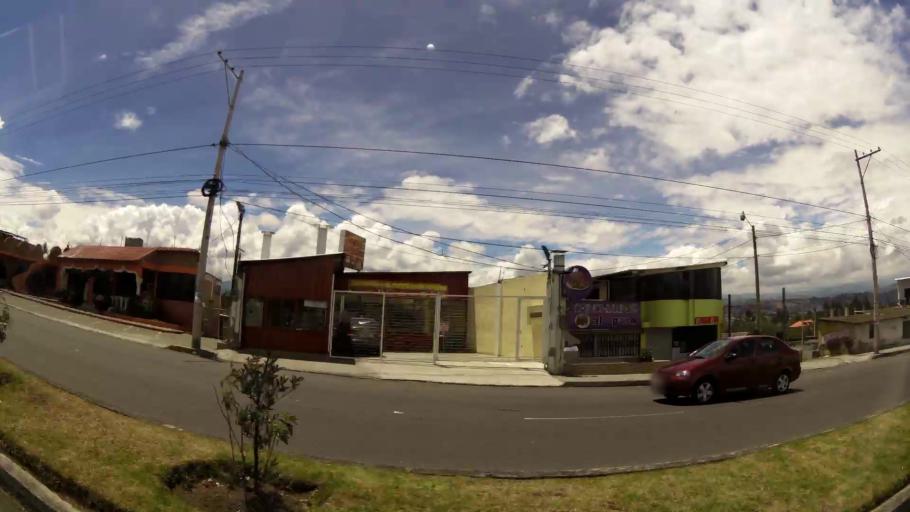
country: EC
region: Tungurahua
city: Ambato
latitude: -1.2994
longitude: -78.6007
